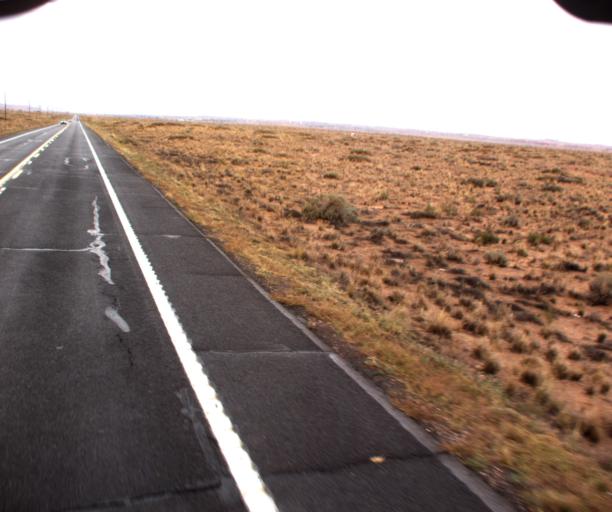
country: US
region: Arizona
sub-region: Coconino County
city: Tuba City
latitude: 36.1403
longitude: -111.1623
